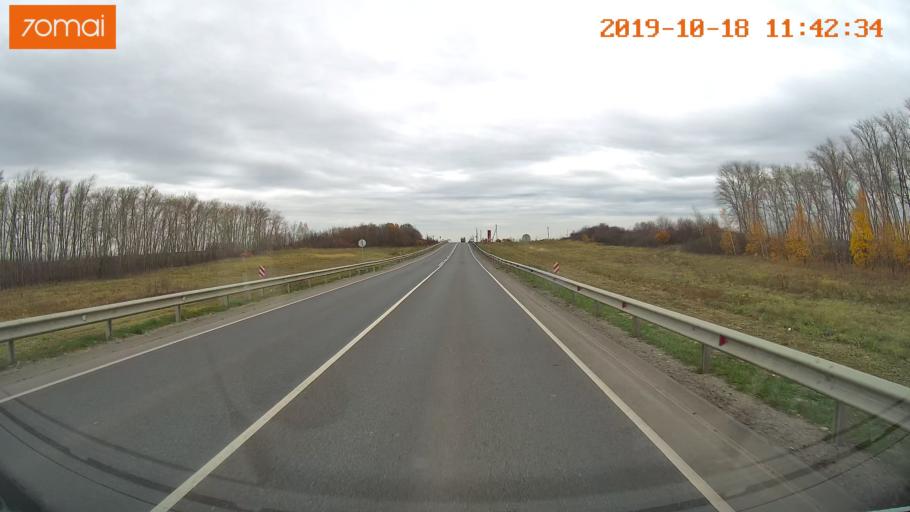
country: RU
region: Rjazan
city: Oktyabr'skiy
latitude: 54.1897
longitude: 38.9306
